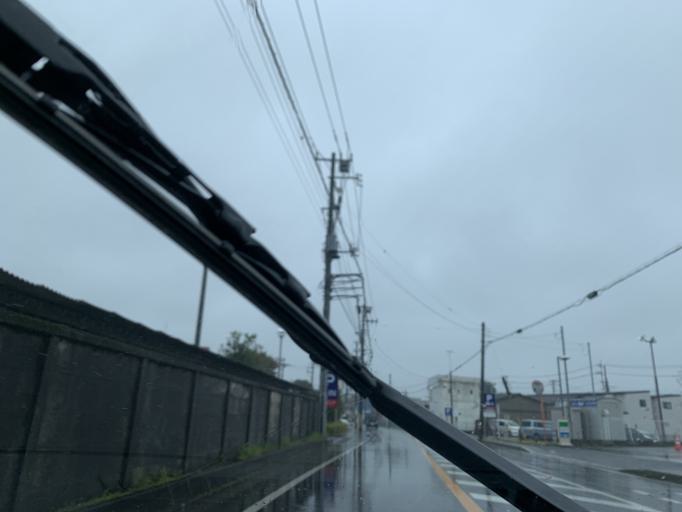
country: JP
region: Chiba
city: Kashiwa
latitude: 35.8812
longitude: 139.9369
